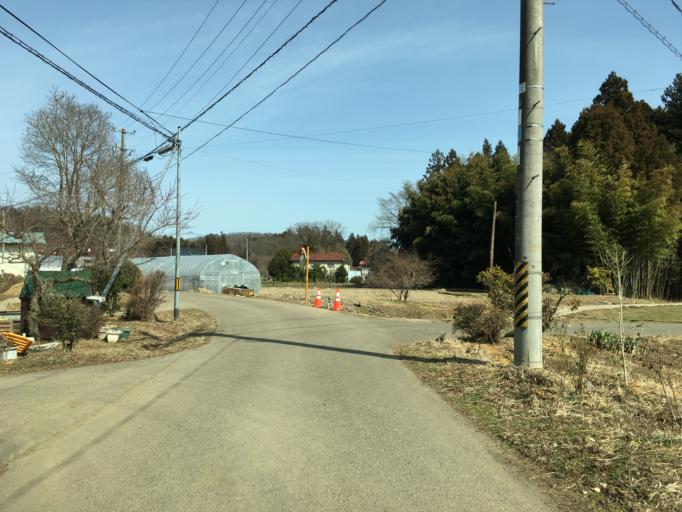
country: JP
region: Fukushima
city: Nihommatsu
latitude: 37.6202
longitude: 140.4205
